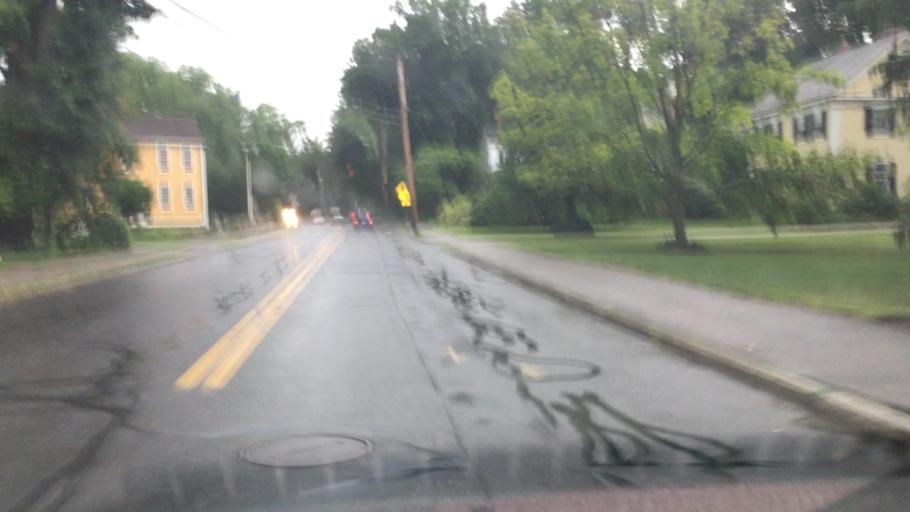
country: US
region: Massachusetts
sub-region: Middlesex County
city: Lexington
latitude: 42.4530
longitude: -71.2286
